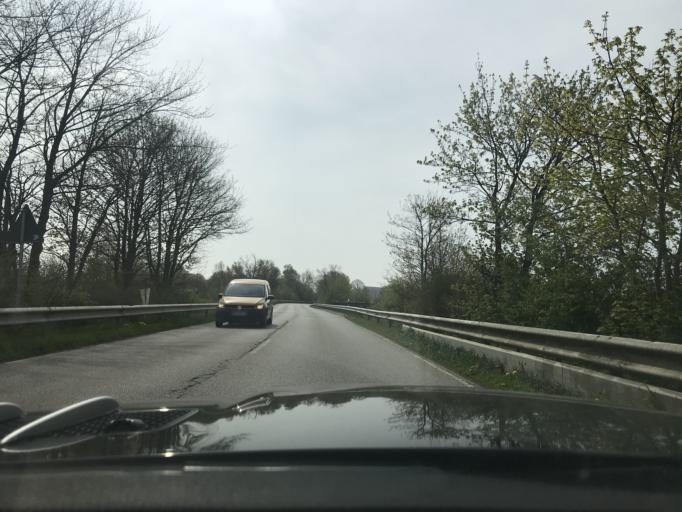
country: DE
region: Schleswig-Holstein
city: Grube
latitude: 54.2423
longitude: 11.0317
